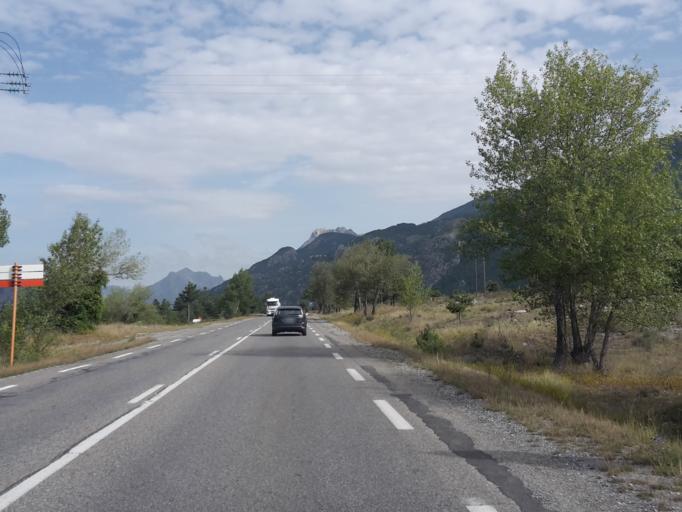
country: FR
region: Provence-Alpes-Cote d'Azur
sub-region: Departement des Hautes-Alpes
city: Guillestre
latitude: 44.6867
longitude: 6.6137
